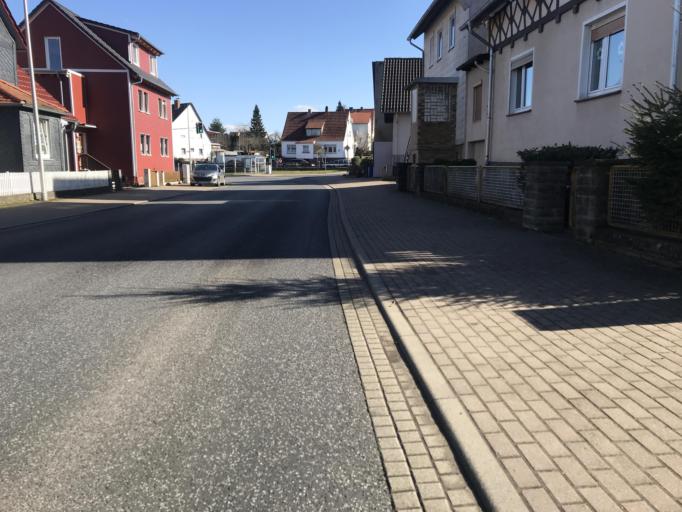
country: DE
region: Hesse
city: Schwalmstadt
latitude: 50.9043
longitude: 9.2172
